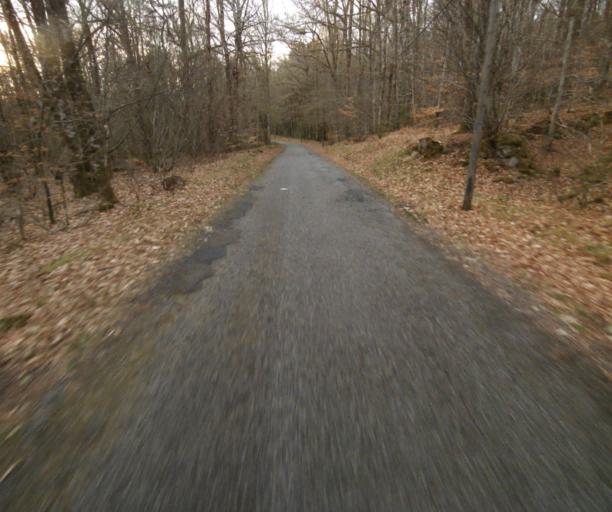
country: FR
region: Limousin
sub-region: Departement de la Correze
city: Correze
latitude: 45.2508
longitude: 1.9741
